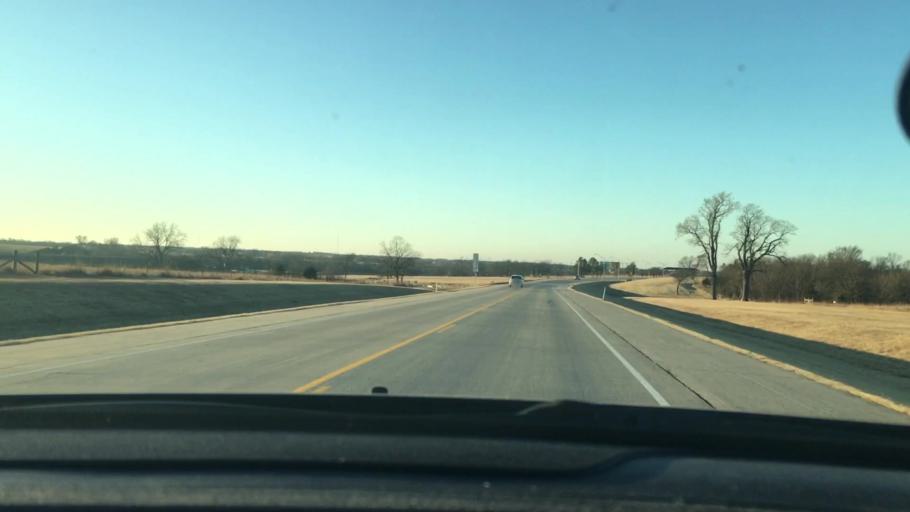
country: US
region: Oklahoma
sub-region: Murray County
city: Sulphur
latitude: 34.5732
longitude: -96.9260
